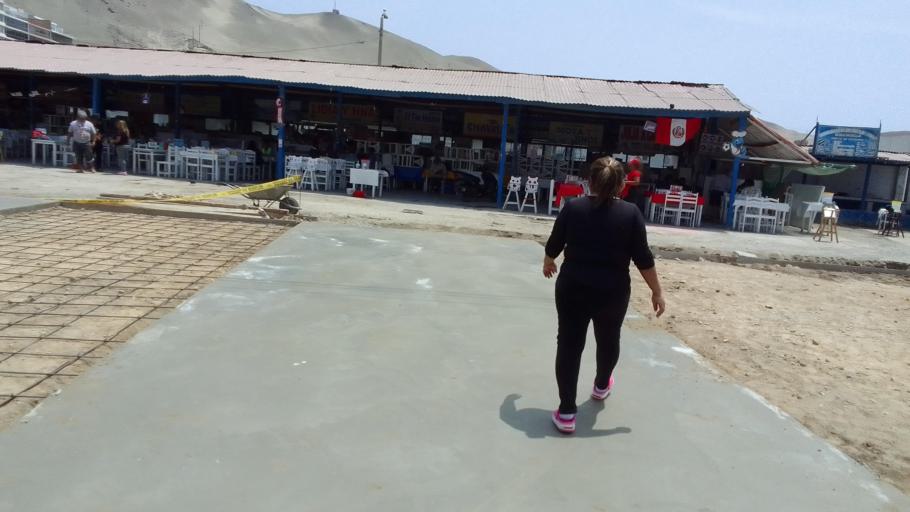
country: PE
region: Lima
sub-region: Lima
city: Santa Rosa
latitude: -11.7727
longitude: -77.1766
